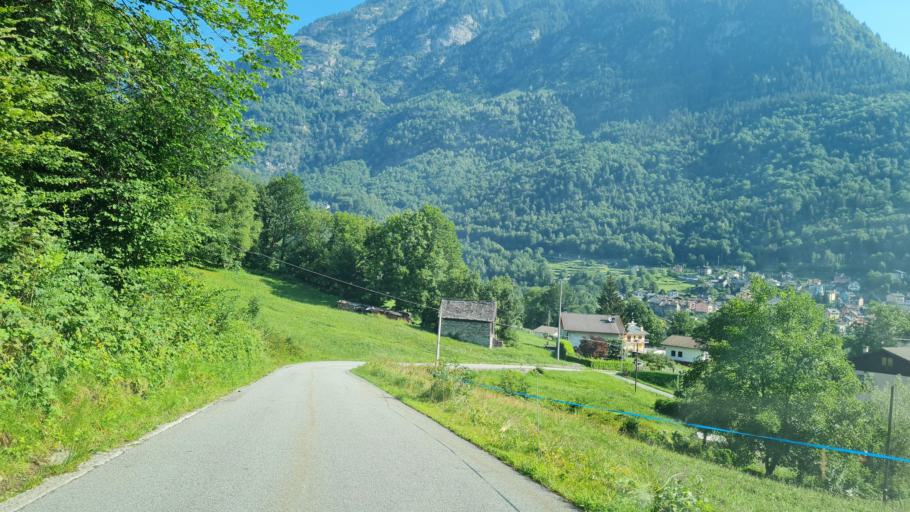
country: IT
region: Piedmont
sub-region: Provincia Verbano-Cusio-Ossola
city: Baceno
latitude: 46.2565
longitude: 8.3134
